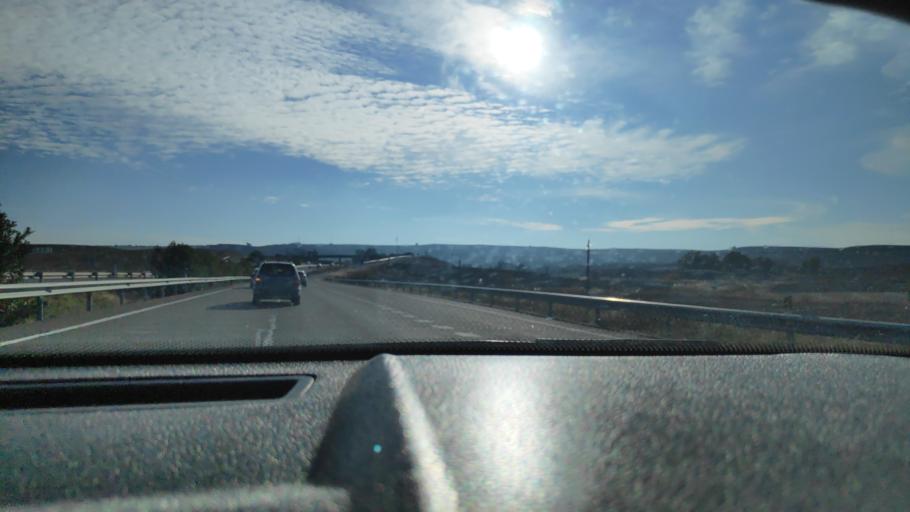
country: ES
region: Andalusia
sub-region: Province of Cordoba
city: Villarrubia
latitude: 37.7883
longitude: -4.8142
